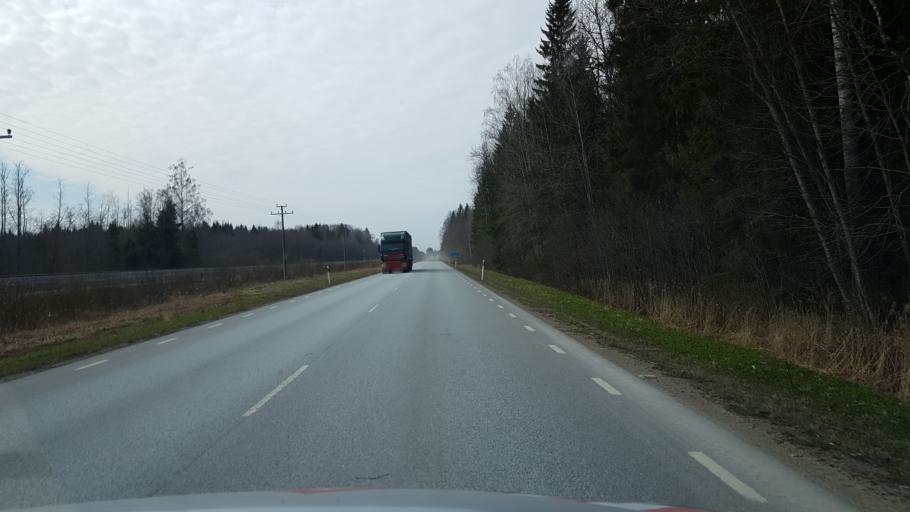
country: EE
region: Ida-Virumaa
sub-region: Aseri vald
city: Aseri
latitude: 59.3485
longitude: 26.8010
